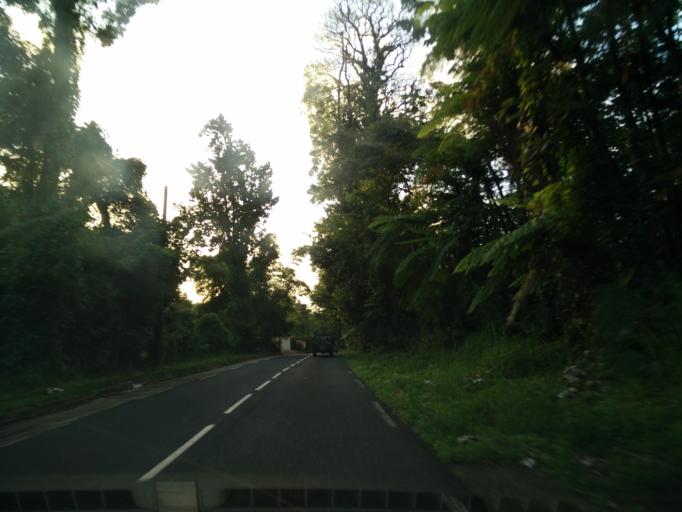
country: MQ
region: Martinique
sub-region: Martinique
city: Le Morne-Rouge
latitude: 14.7510
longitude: -61.1052
